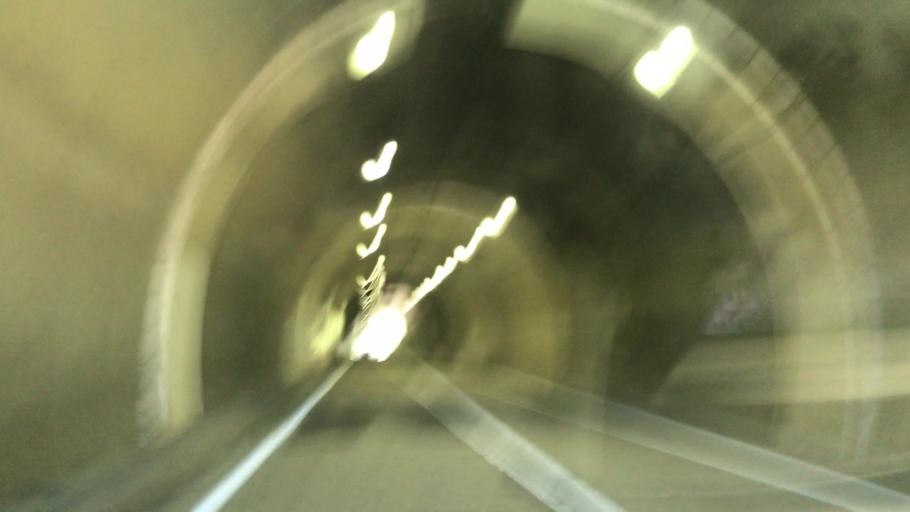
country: JP
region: Hokkaido
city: Shimo-furano
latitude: 42.9633
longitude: 142.6447
